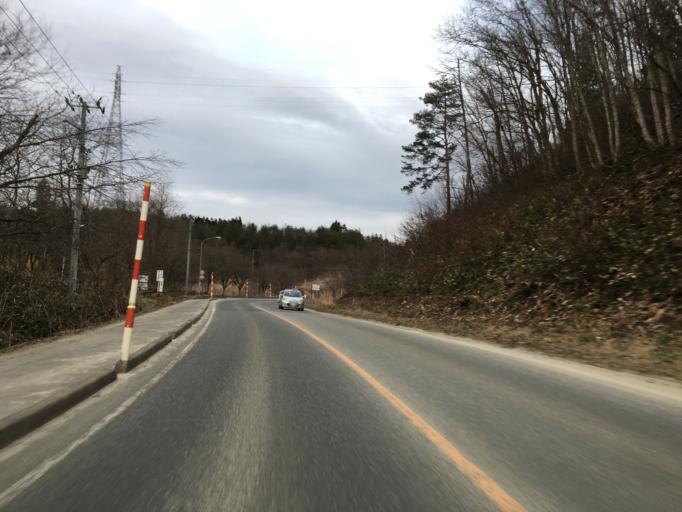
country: JP
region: Yamagata
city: Nagai
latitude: 38.0967
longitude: 140.0553
